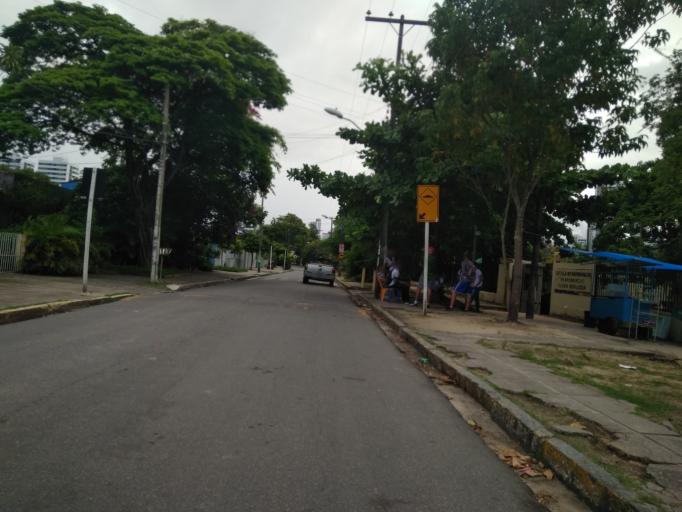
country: BR
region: Pernambuco
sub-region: Recife
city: Recife
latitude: -8.0329
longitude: -34.8868
